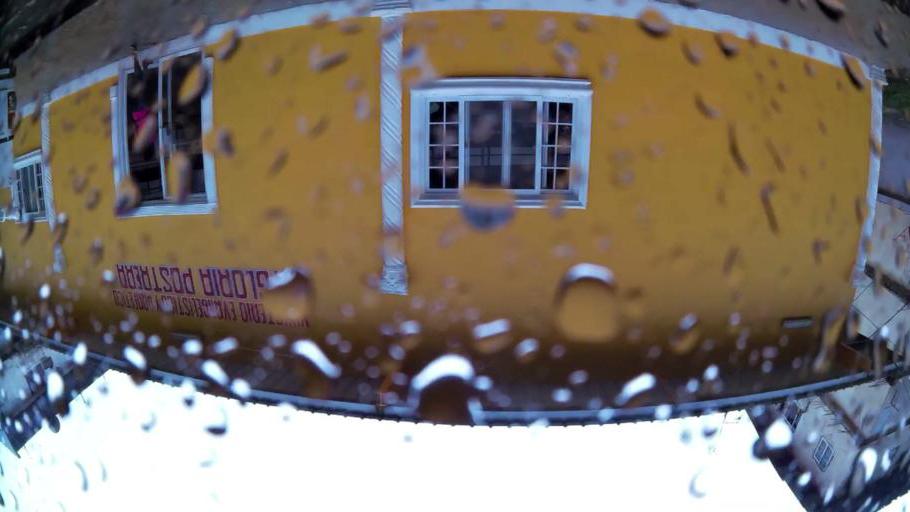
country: PA
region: Colon
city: Colon
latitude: 9.3625
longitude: -79.9058
